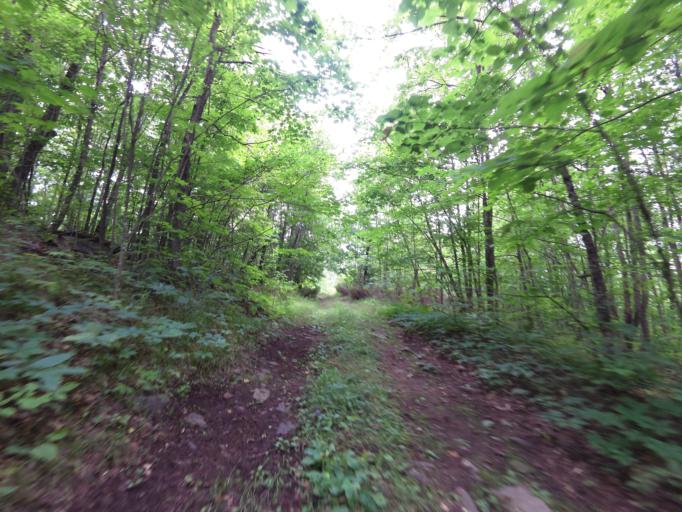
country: CA
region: Ontario
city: Perth
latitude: 44.8220
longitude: -76.5770
